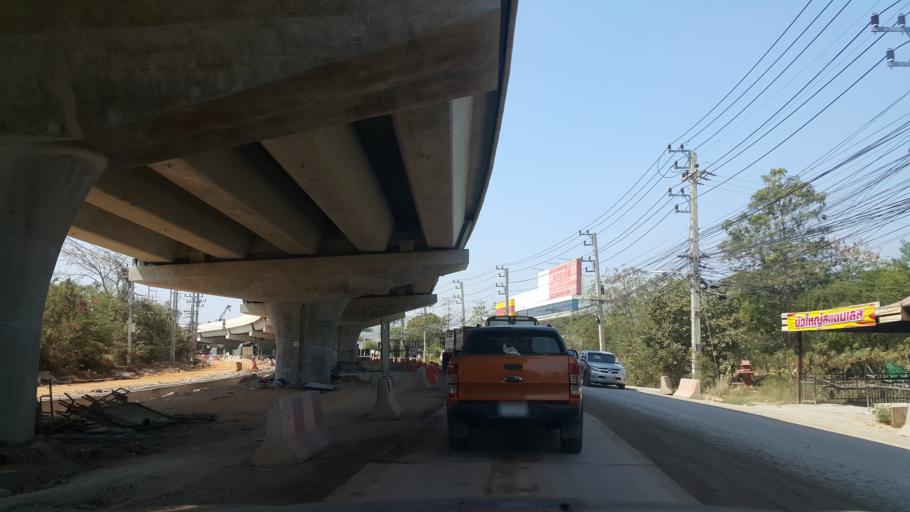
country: TH
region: Nakhon Ratchasima
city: Bua Yai
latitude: 15.5922
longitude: 102.4313
